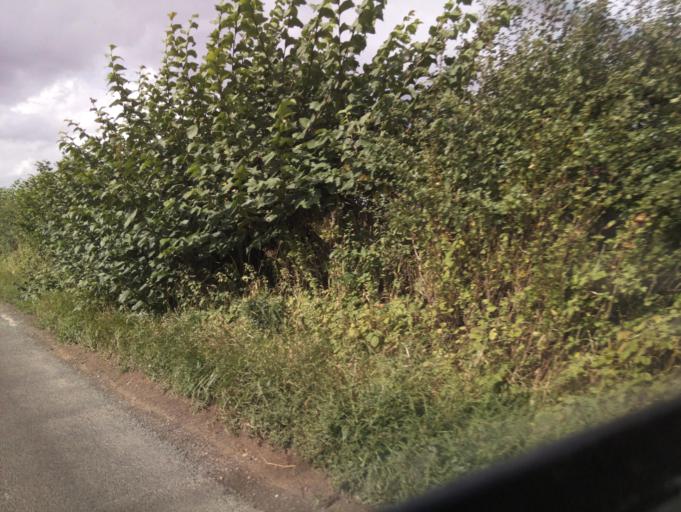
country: GB
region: England
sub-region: North Yorkshire
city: Bedale
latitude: 54.2126
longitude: -1.6252
